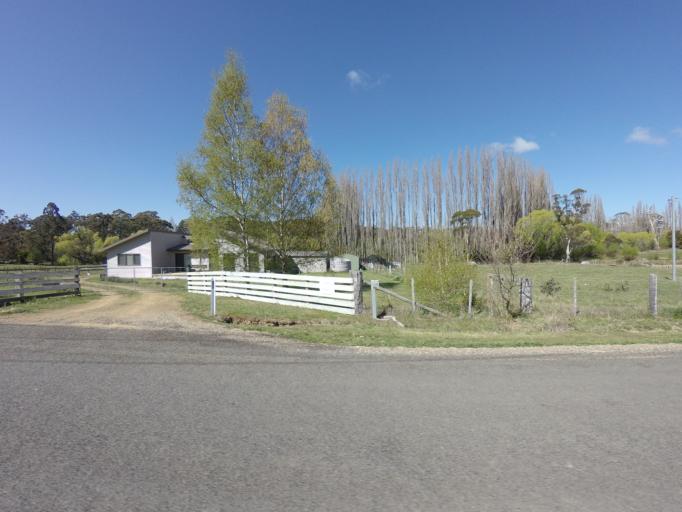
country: AU
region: Tasmania
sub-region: Derwent Valley
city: New Norfolk
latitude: -42.6050
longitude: 146.7060
